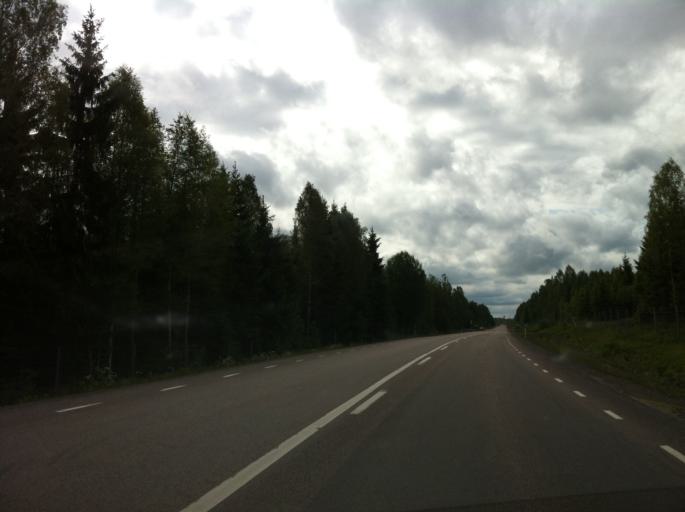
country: SE
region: Vaermland
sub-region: Sunne Kommun
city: Sunne
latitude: 59.7640
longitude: 13.1108
